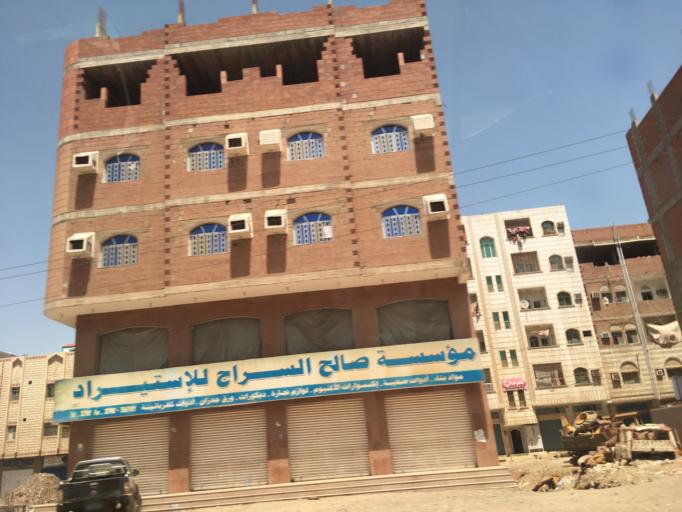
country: YE
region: Aden
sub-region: Al Mansura
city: Al Mansurah
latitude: 12.8648
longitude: 44.9714
